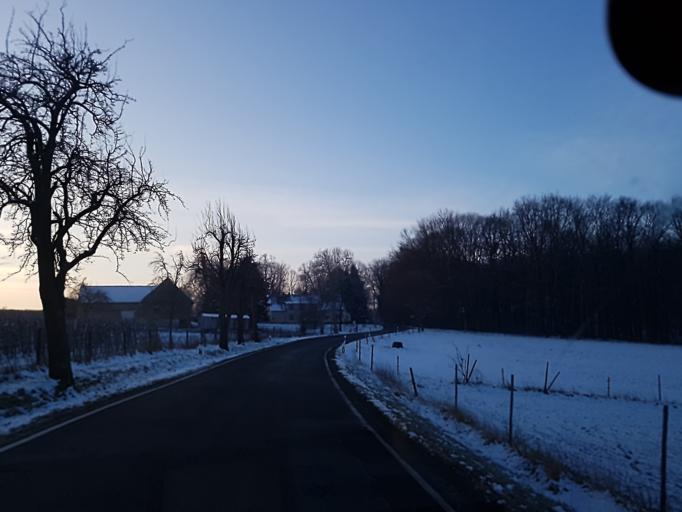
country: DE
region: Saxony
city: Mugeln
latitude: 51.2209
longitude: 13.0327
